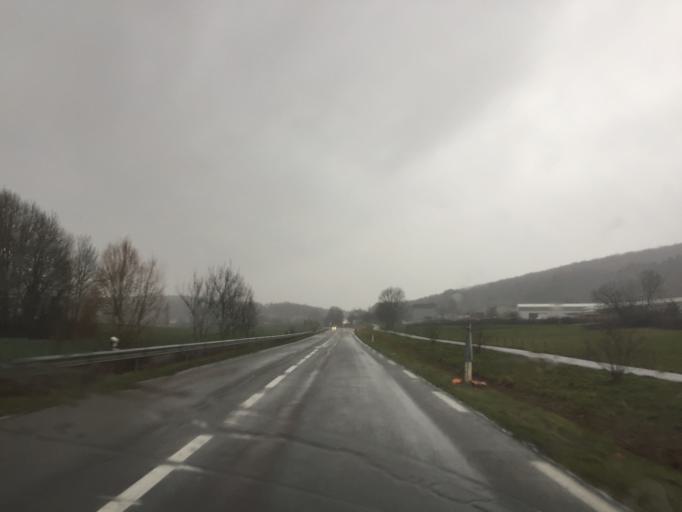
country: FR
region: Franche-Comte
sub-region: Departement du Jura
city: Mouchard
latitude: 46.9845
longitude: 5.8178
